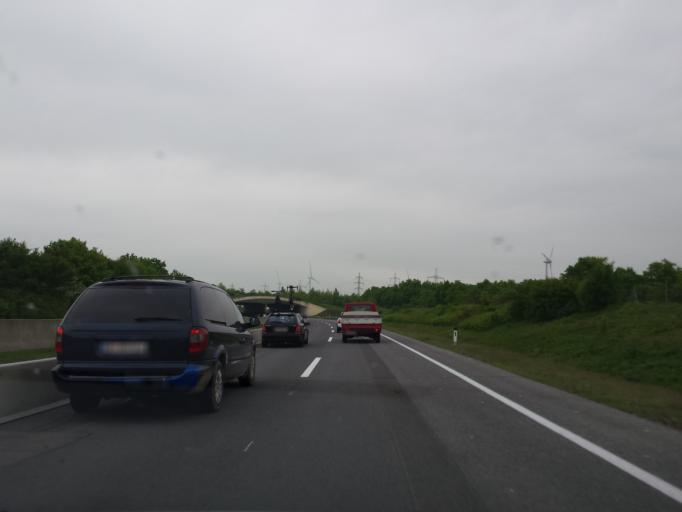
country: AT
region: Burgenland
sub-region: Politischer Bezirk Neusiedl am See
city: Weiden am See
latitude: 47.9628
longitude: 16.9095
